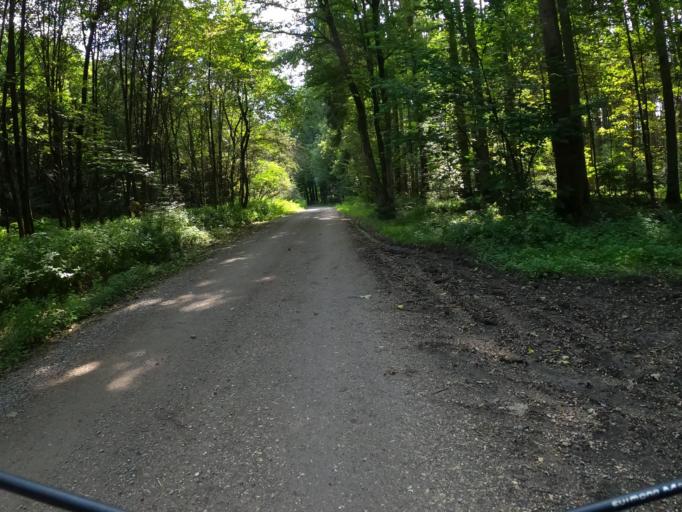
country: DE
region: Bavaria
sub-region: Swabia
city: Rieden an der Kotz
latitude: 48.3730
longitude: 10.2276
